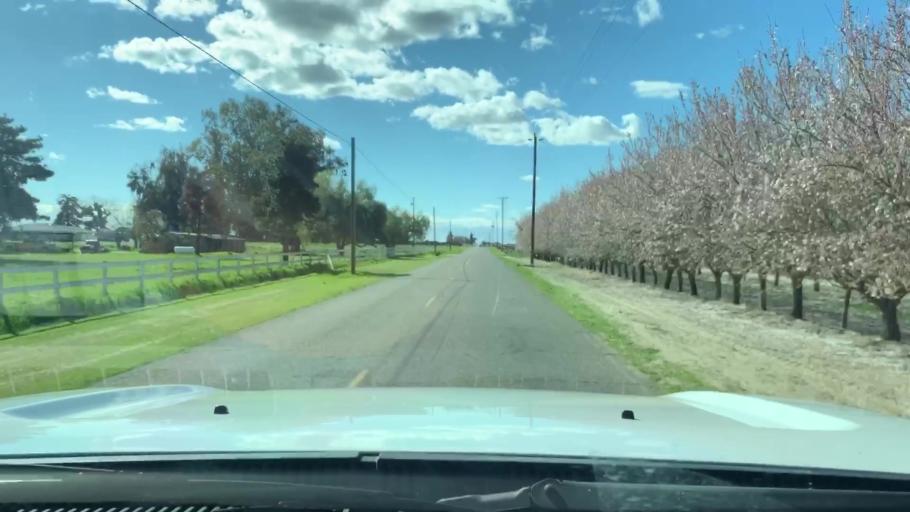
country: US
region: California
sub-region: Fresno County
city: Fowler
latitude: 36.5618
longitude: -119.7125
